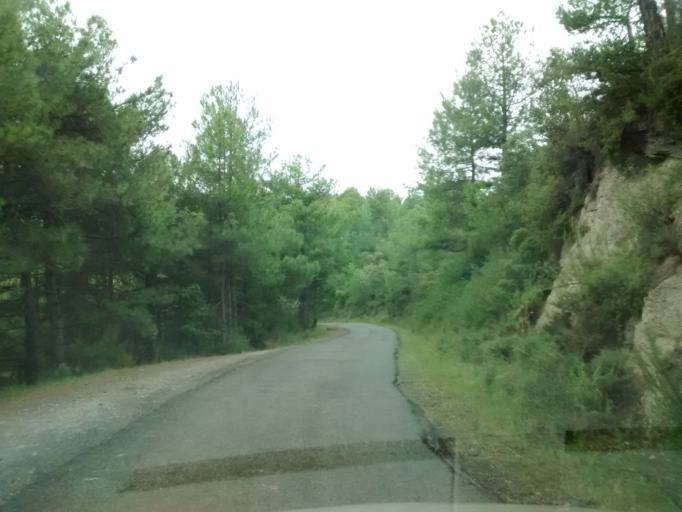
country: ES
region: Aragon
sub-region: Provincia de Huesca
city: Puertolas
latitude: 42.5253
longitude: 0.1317
